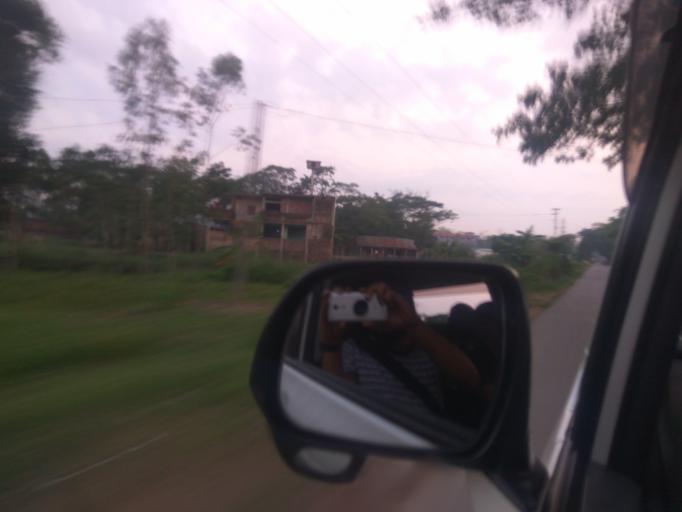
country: IN
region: Assam
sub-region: Karimganj
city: Karimganj
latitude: 24.9439
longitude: 92.2322
